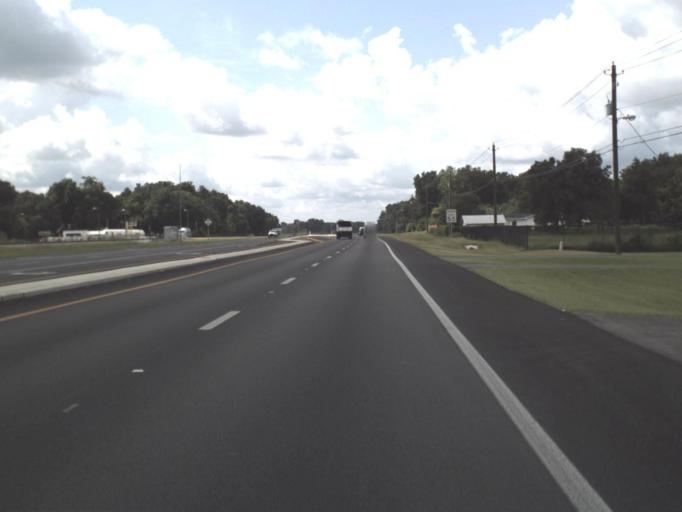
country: US
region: Florida
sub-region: Hillsborough County
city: Plant City
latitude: 28.0758
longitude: -82.1379
